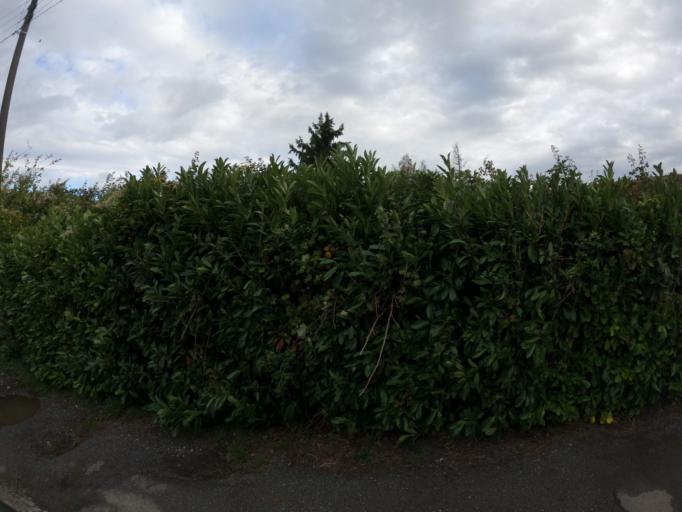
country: FR
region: Ile-de-France
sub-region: Departement de Seine-et-Marne
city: Montry
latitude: 48.8728
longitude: 2.8338
